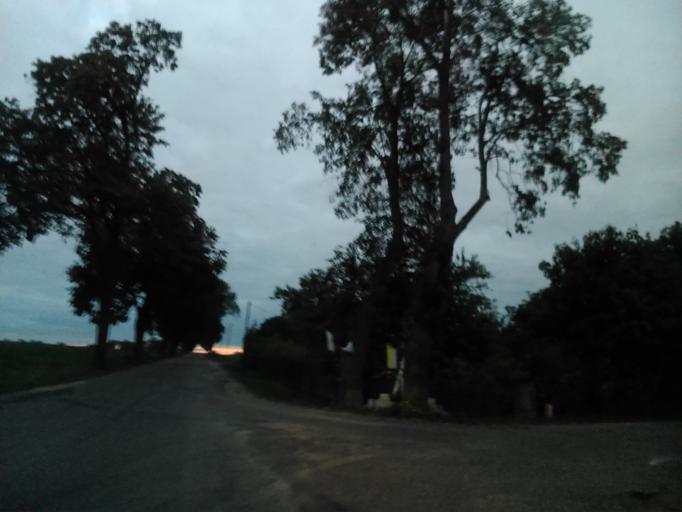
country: PL
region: Kujawsko-Pomorskie
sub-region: Powiat golubsko-dobrzynski
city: Kowalewo Pomorskie
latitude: 53.1215
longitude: 18.9133
